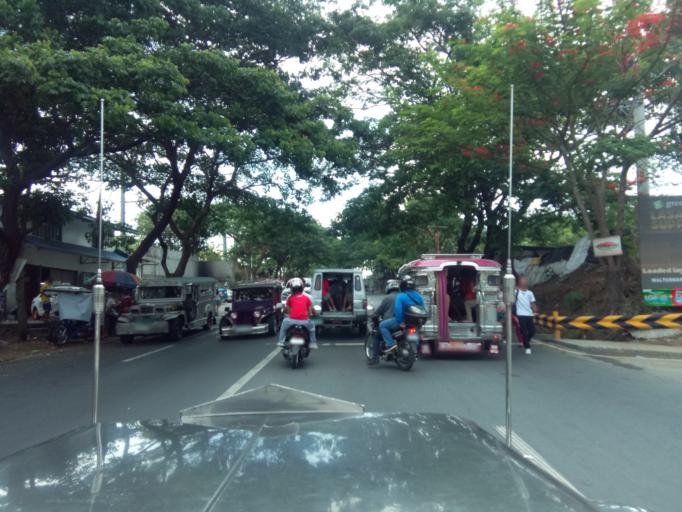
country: PH
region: Calabarzon
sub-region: Province of Cavite
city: Aliang
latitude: 14.2801
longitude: 120.8820
